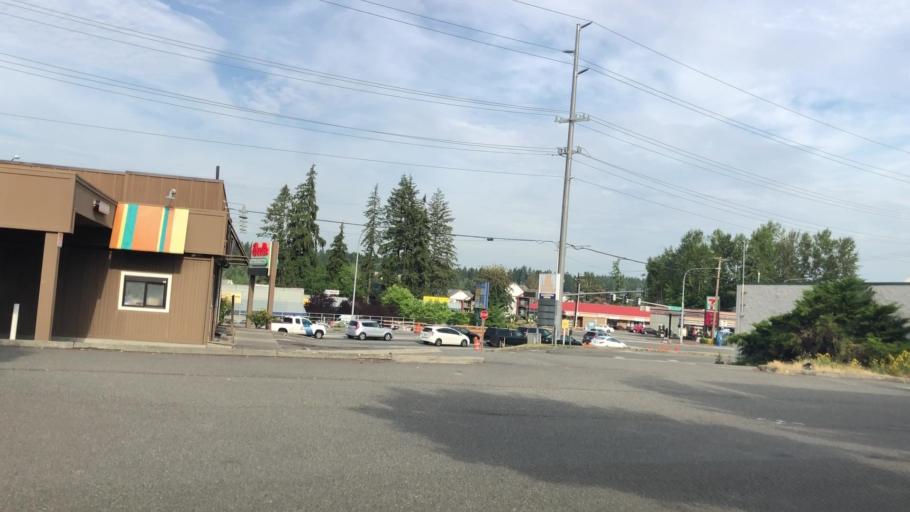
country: US
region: Washington
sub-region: Snohomish County
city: Mill Creek
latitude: 47.8341
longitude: -122.2094
